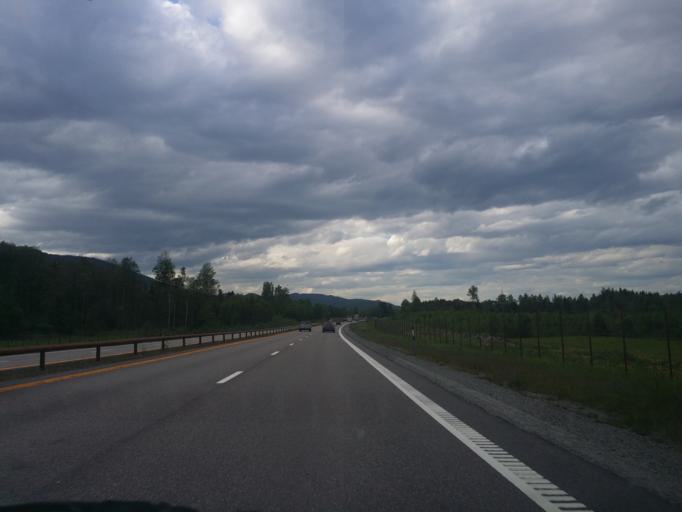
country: NO
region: Akershus
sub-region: Eidsvoll
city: Eidsvoll
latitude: 60.3579
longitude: 11.2057
